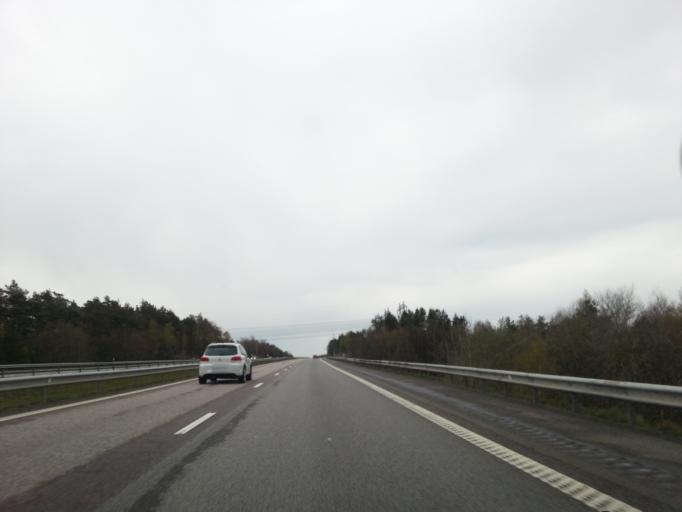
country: SE
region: Halland
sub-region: Kungsbacka Kommun
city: Frillesas
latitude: 57.2864
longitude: 12.2159
